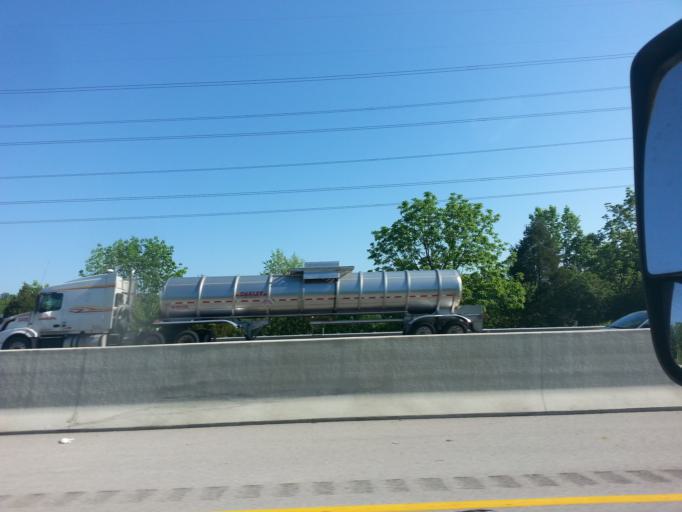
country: US
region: Kentucky
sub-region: Jefferson County
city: Middletown
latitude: 38.2220
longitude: -85.4856
